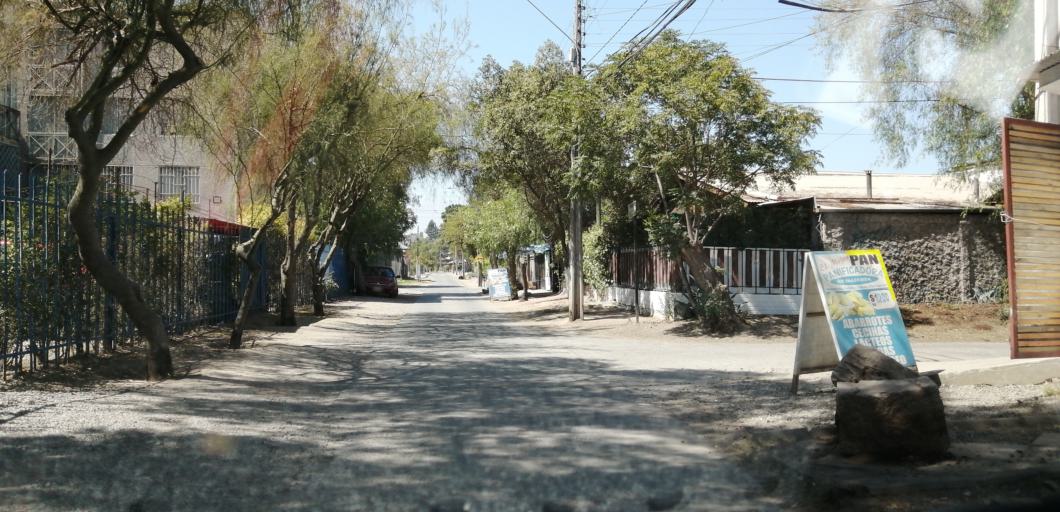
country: CL
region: Santiago Metropolitan
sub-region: Provincia de Santiago
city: Lo Prado
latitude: -33.4450
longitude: -70.7489
